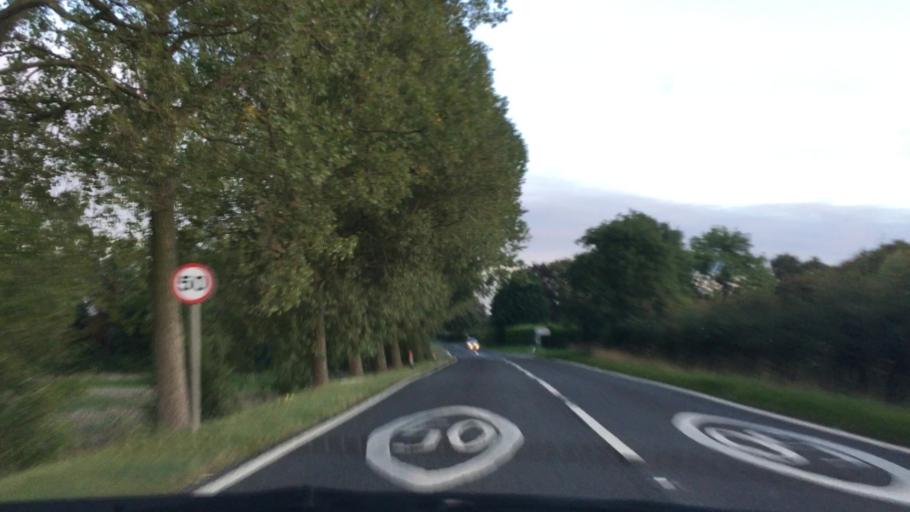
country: GB
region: England
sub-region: North East Lincolnshire
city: Wold Newton
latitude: 53.4662
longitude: -0.1038
